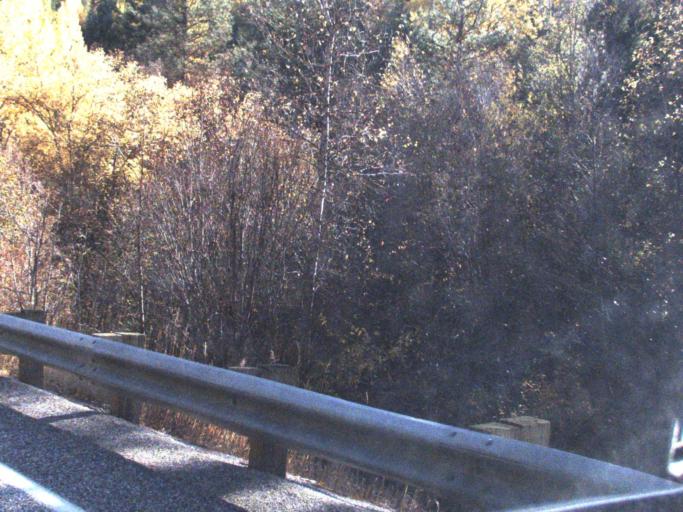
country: US
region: Washington
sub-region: Stevens County
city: Kettle Falls
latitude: 48.5847
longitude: -118.2075
